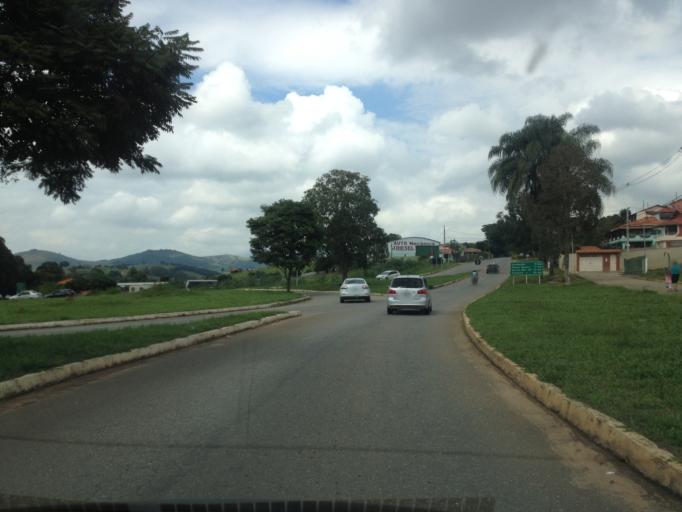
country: BR
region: Minas Gerais
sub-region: Itanhandu
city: Itanhandu
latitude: -22.2529
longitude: -44.9315
